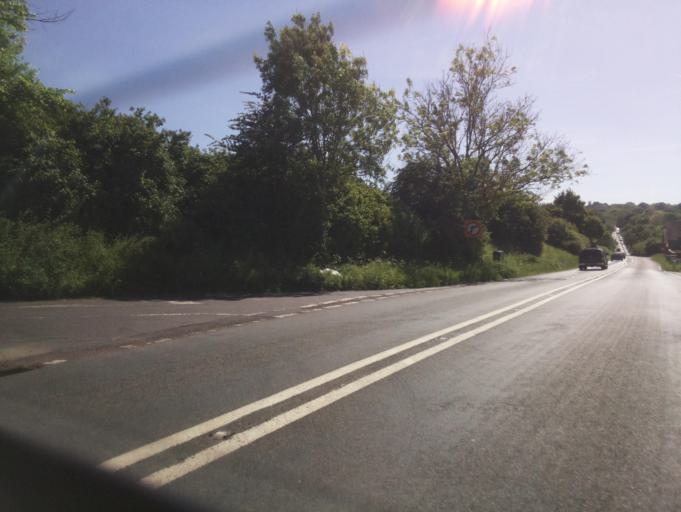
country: GB
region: England
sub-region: Somerset
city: Crewkerne
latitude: 50.8957
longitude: -2.7687
